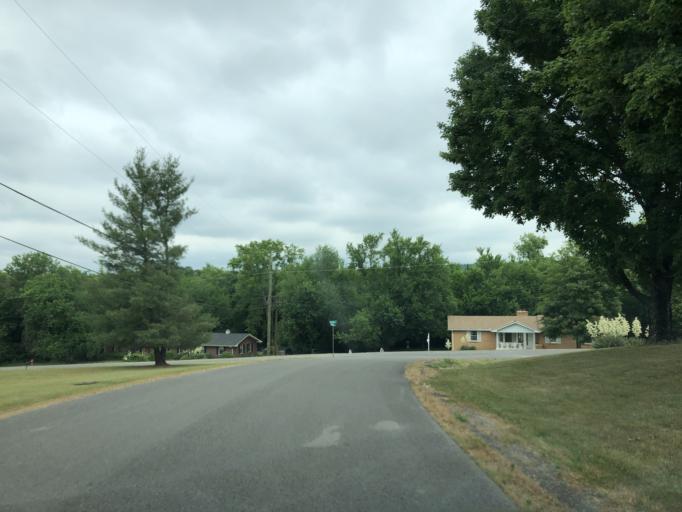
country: US
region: Tennessee
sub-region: Davidson County
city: Goodlettsville
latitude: 36.2807
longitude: -86.7633
